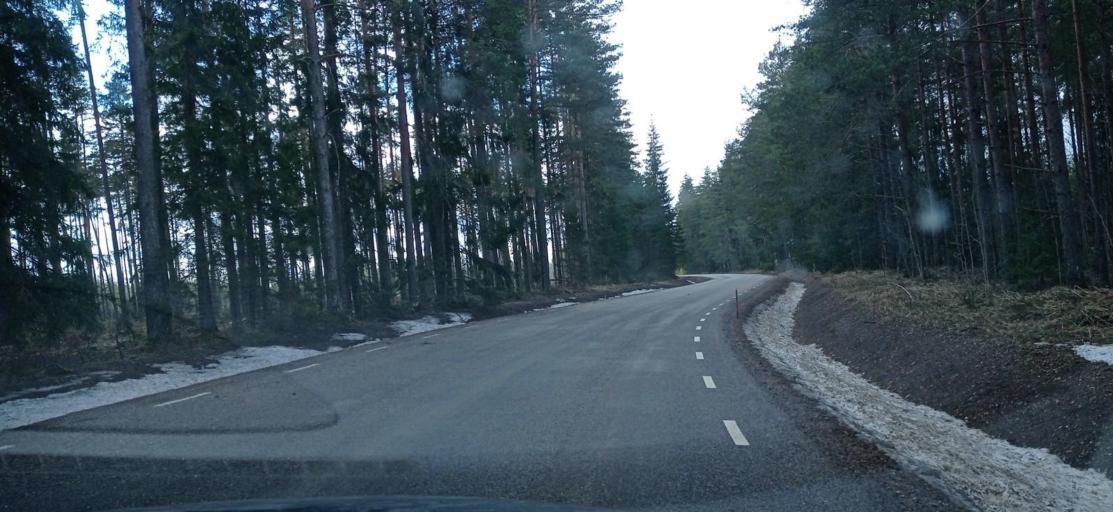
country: EE
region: Polvamaa
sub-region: Polva linn
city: Polva
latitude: 58.1546
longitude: 27.0563
